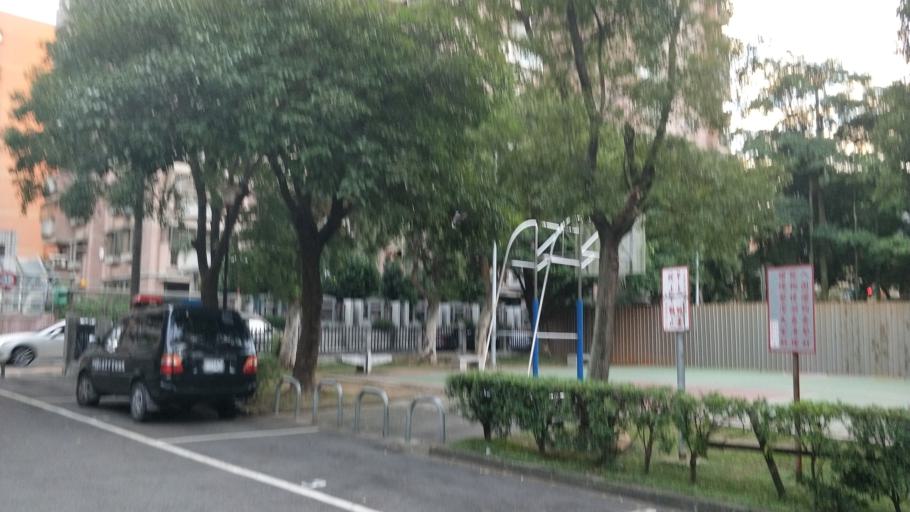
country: TW
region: Taiwan
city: Taoyuan City
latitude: 24.9725
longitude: 121.2334
